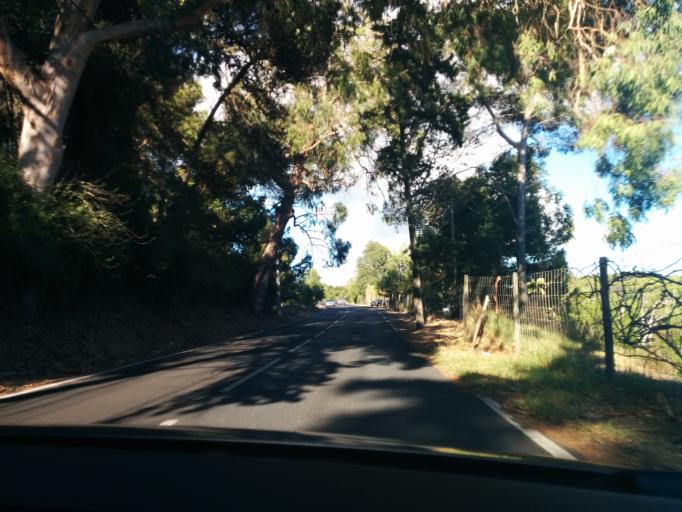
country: PT
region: Lisbon
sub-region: Cascais
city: Alcabideche
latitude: 38.7342
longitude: -9.4636
